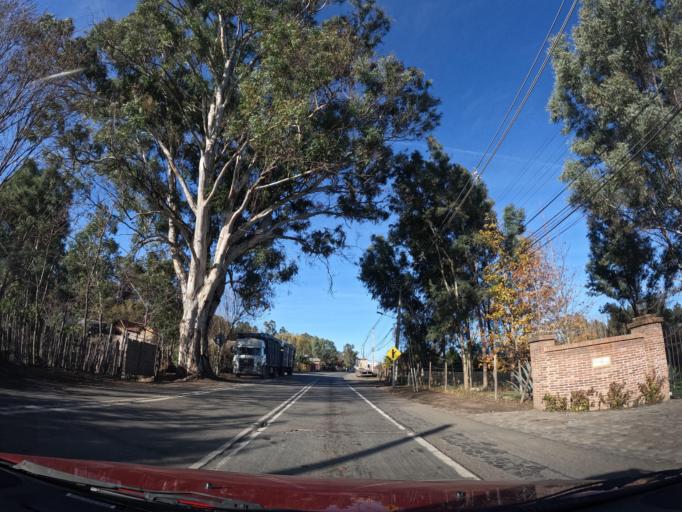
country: CL
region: Maule
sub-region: Provincia de Linares
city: San Javier
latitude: -35.5711
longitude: -71.6948
